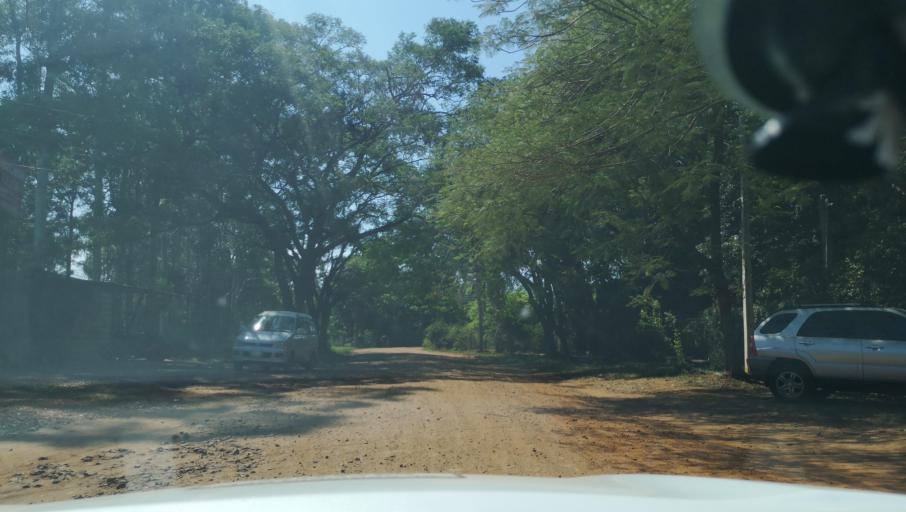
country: PY
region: Itapua
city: Carmen del Parana
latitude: -27.1591
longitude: -56.2480
